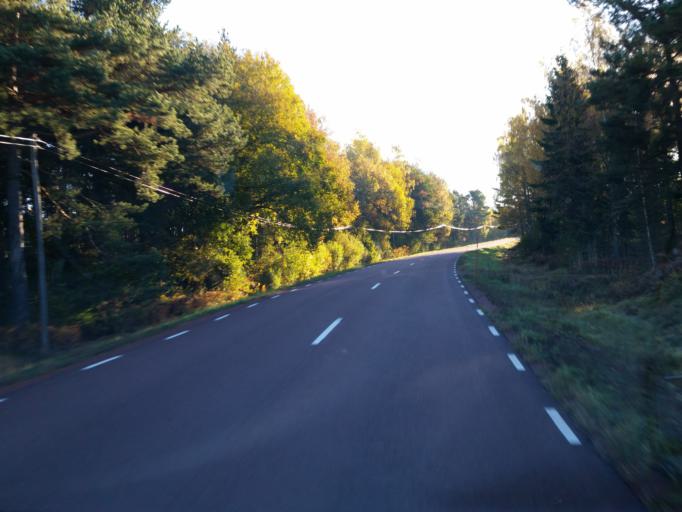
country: AX
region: Alands skaergard
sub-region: Vardoe
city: Vardoe
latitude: 60.2301
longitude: 20.3929
